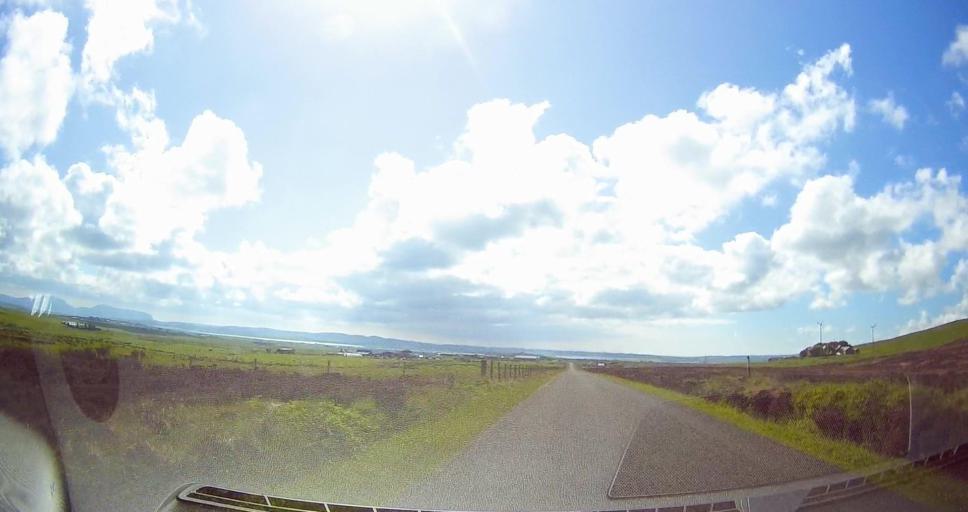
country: GB
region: Scotland
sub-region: Orkney Islands
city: Stromness
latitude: 59.0469
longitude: -3.1407
